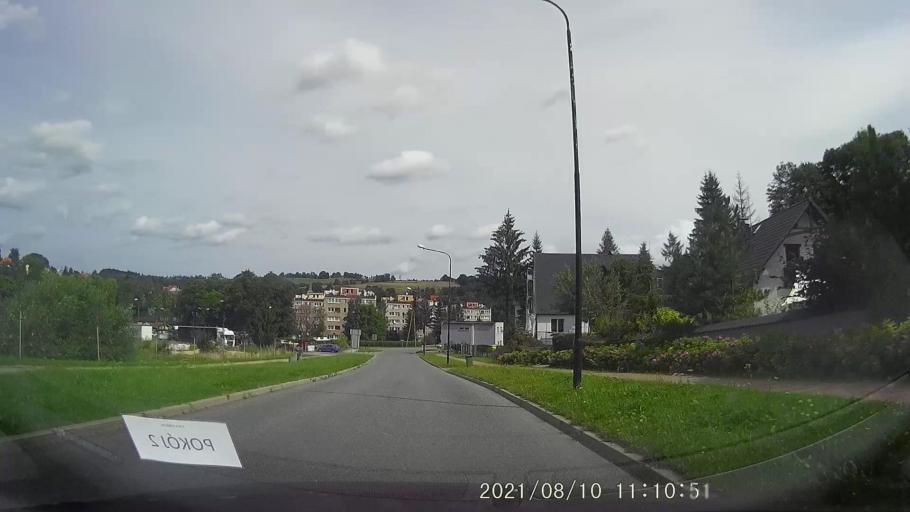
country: PL
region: Lower Silesian Voivodeship
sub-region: Powiat klodzki
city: Duszniki-Zdroj
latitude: 50.4003
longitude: 16.3943
